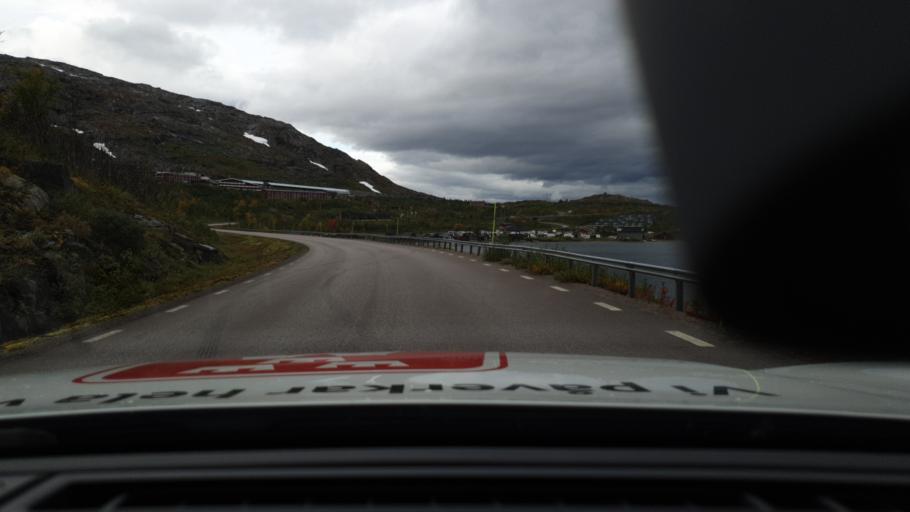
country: NO
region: Troms
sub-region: Lavangen
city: Tennevoll
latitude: 68.4278
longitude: 18.1430
